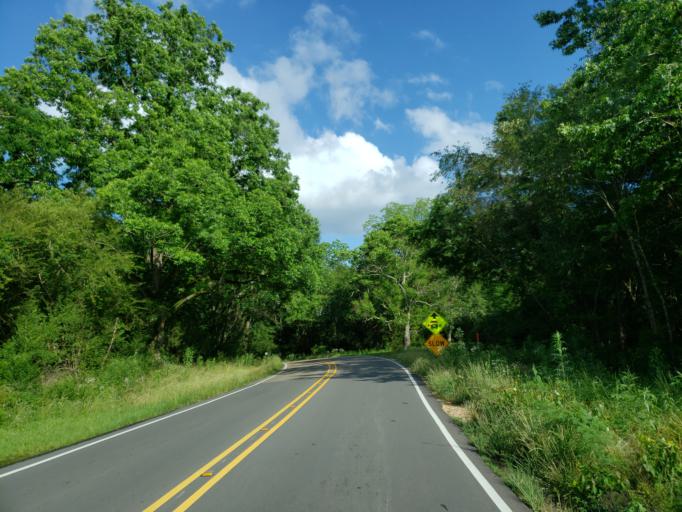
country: US
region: Mississippi
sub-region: Lamar County
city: West Hattiesburg
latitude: 31.2710
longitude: -89.4115
